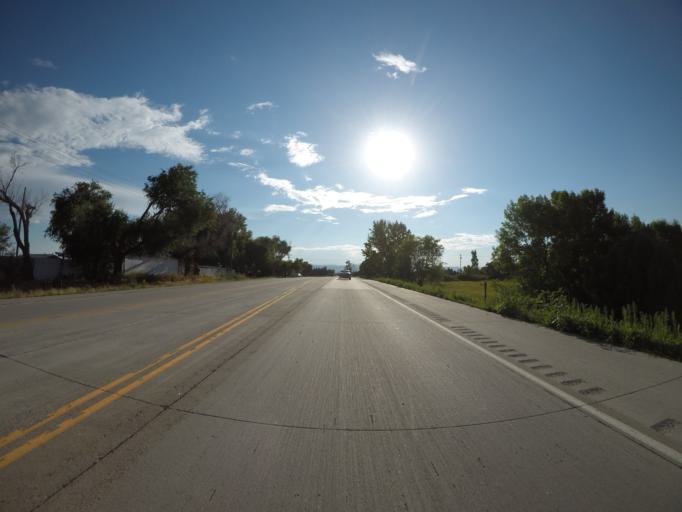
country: US
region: Colorado
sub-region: Weld County
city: Windsor
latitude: 40.5810
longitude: -104.9615
